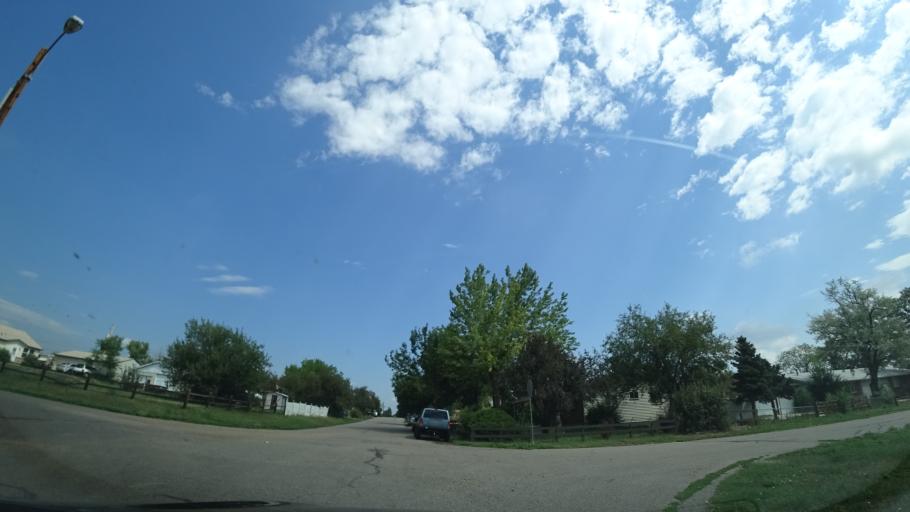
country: US
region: Colorado
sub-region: Jefferson County
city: Lakewood
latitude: 39.7133
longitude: -105.0697
